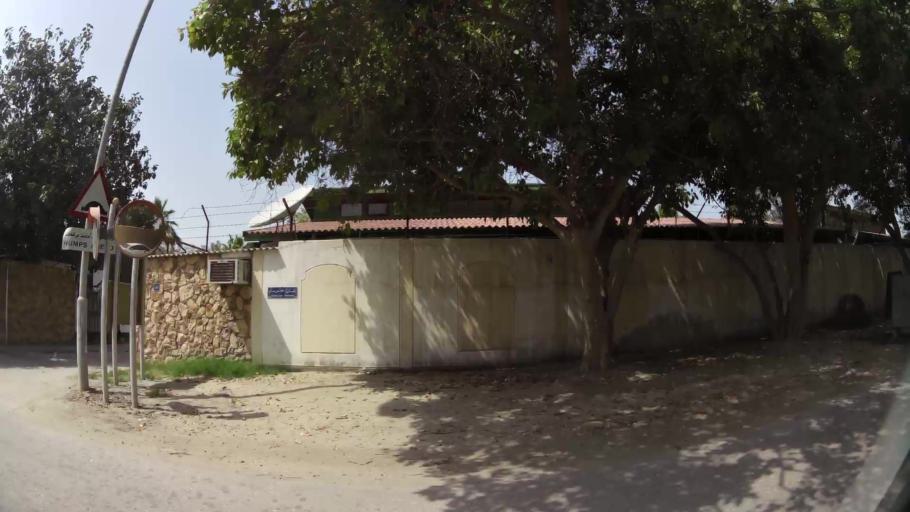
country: BH
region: Manama
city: Jidd Hafs
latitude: 26.2274
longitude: 50.4949
